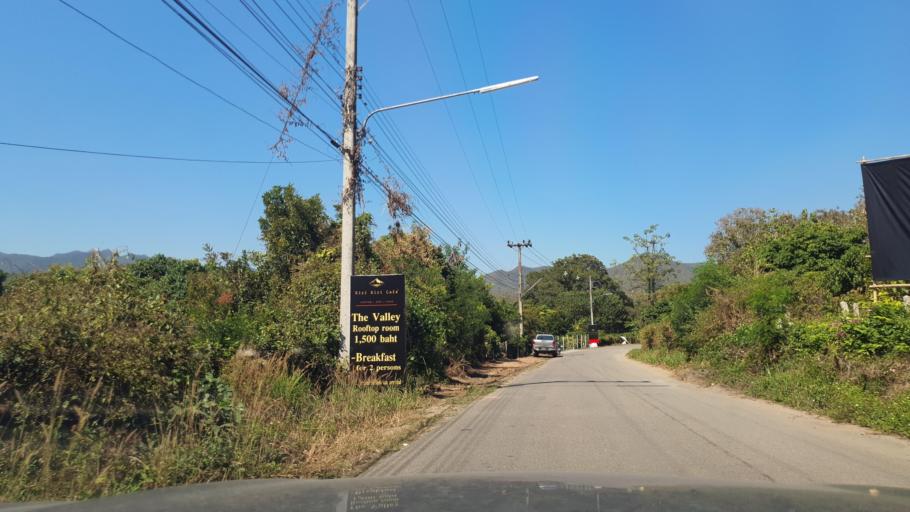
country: TH
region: Chiang Mai
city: Mae Wang
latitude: 18.6809
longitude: 98.8155
